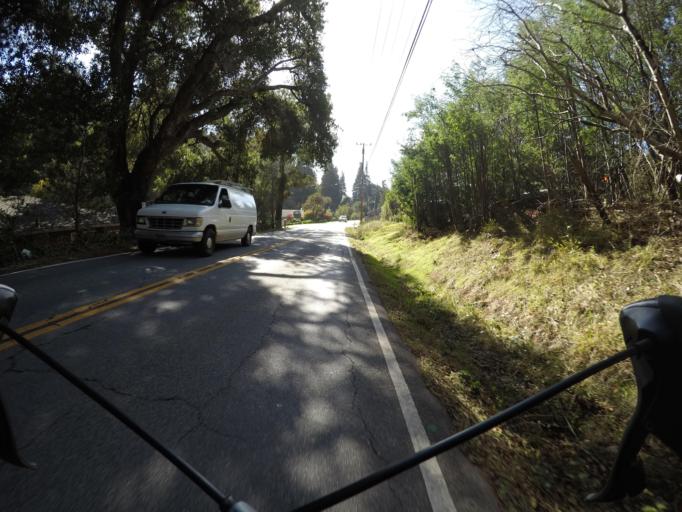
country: US
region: California
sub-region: Santa Cruz County
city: Pasatiempo
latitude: 37.0149
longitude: -121.9989
